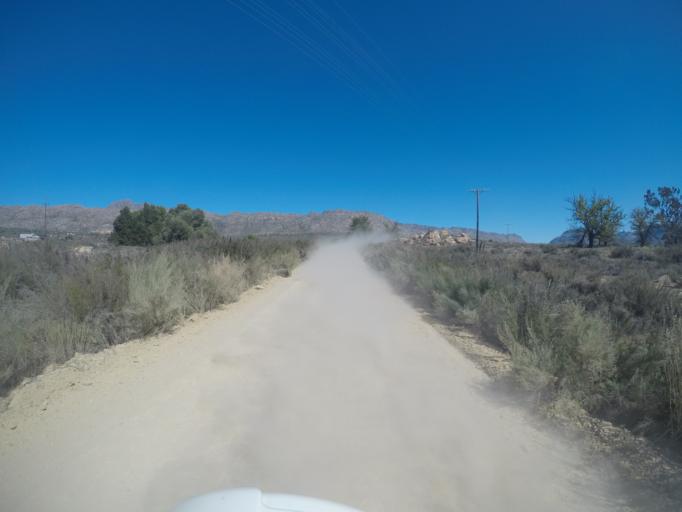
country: ZA
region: Western Cape
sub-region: West Coast District Municipality
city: Clanwilliam
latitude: -32.4693
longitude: 19.2062
